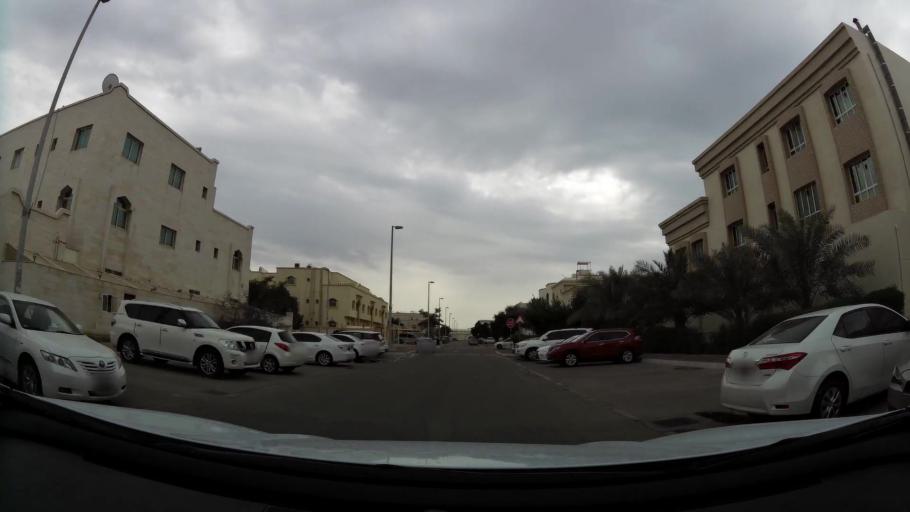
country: AE
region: Abu Dhabi
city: Abu Dhabi
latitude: 24.4263
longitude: 54.4256
